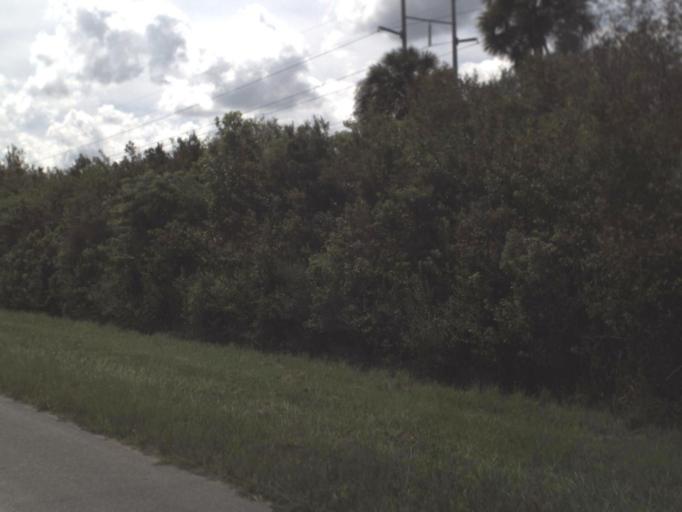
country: US
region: Florida
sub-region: Collier County
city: Orangetree
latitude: 26.0669
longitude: -81.3446
